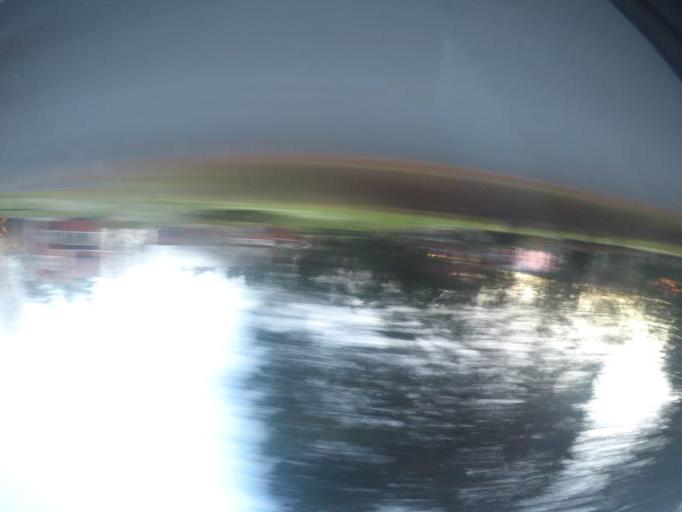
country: SE
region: OErebro
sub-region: Lindesbergs Kommun
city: Frovi
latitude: 59.3214
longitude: 15.4175
